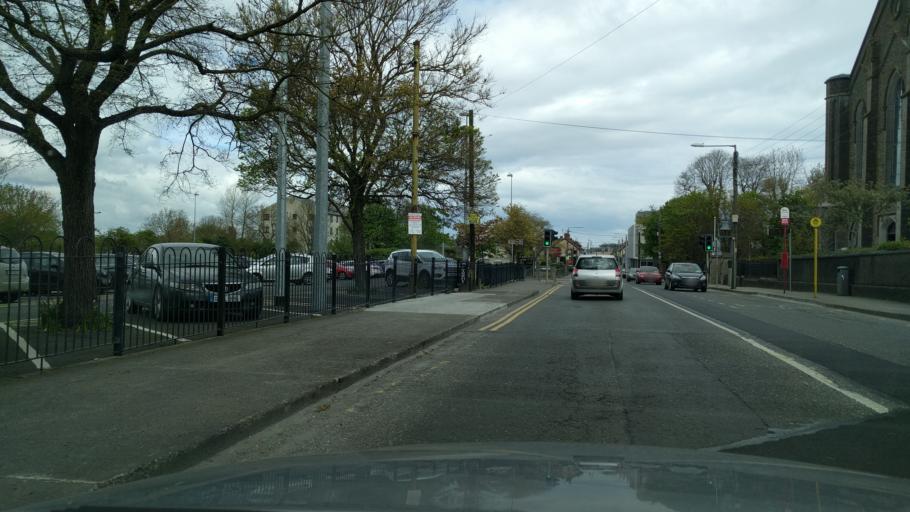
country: IE
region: Leinster
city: Balbriggan
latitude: 53.6037
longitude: -6.1846
